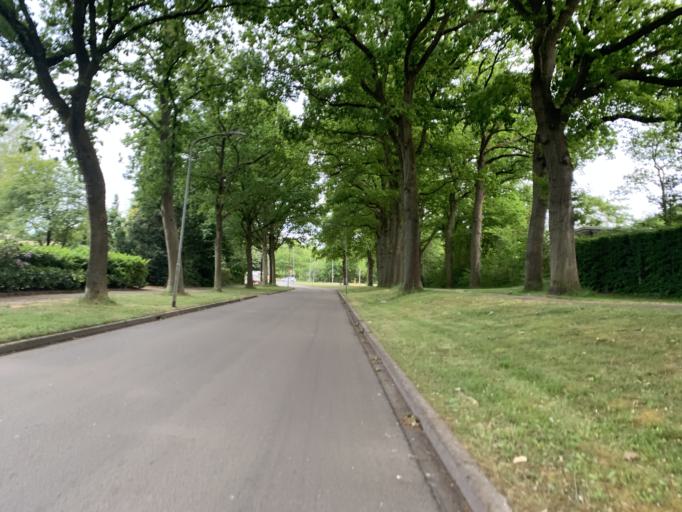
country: NL
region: Groningen
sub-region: Gemeente Haren
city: Haren
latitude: 53.1630
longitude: 6.6167
